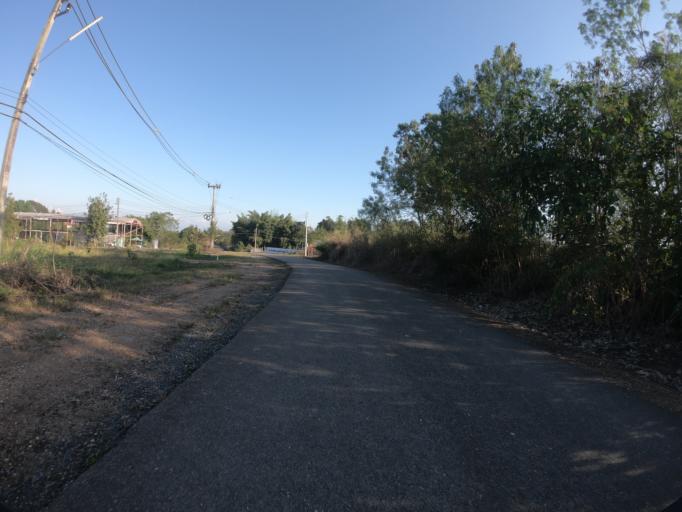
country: TH
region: Chiang Mai
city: Chiang Mai
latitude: 18.7593
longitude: 98.9339
